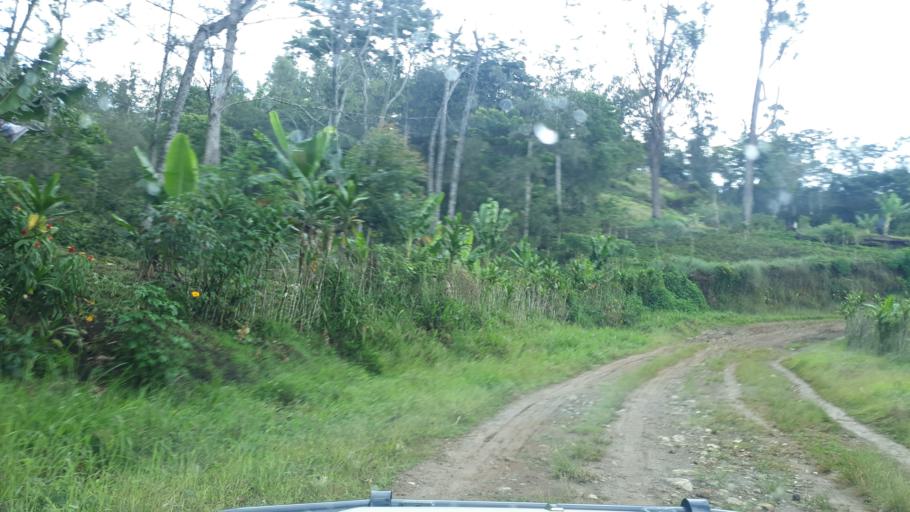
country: PG
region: Eastern Highlands
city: Goroka
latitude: -5.9195
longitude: 145.2550
